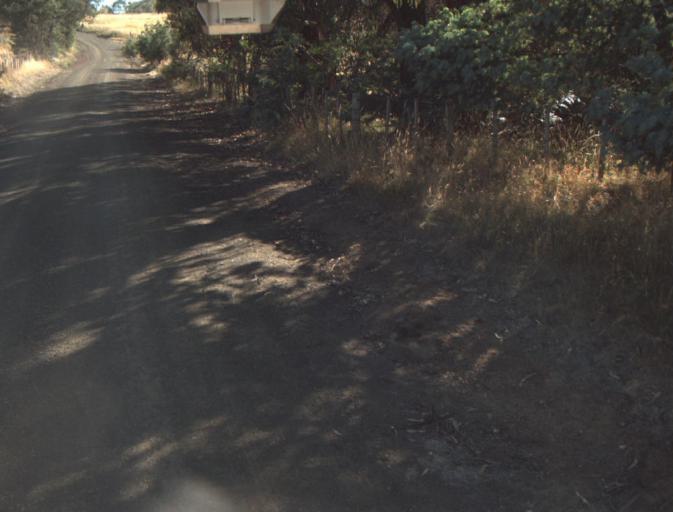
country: AU
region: Tasmania
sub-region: Launceston
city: Newstead
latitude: -41.4121
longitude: 147.2874
